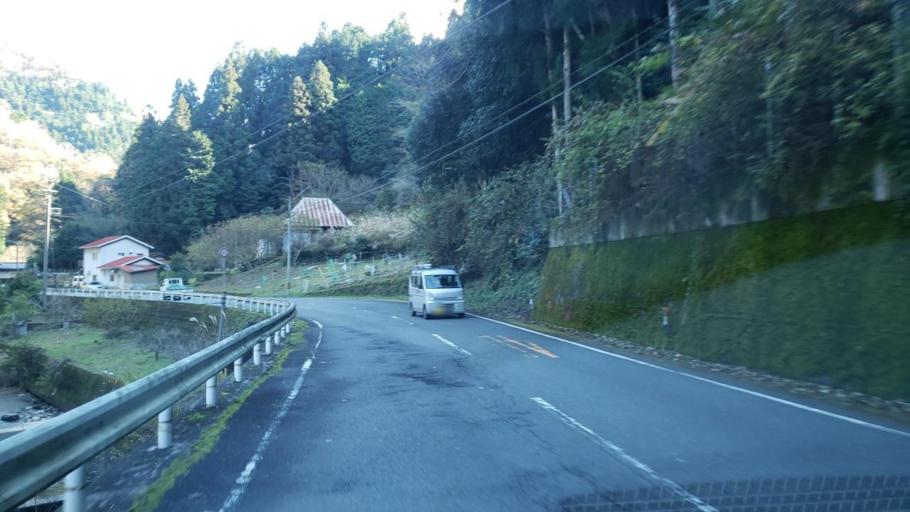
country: JP
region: Tokushima
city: Wakimachi
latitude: 34.0078
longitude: 134.0318
